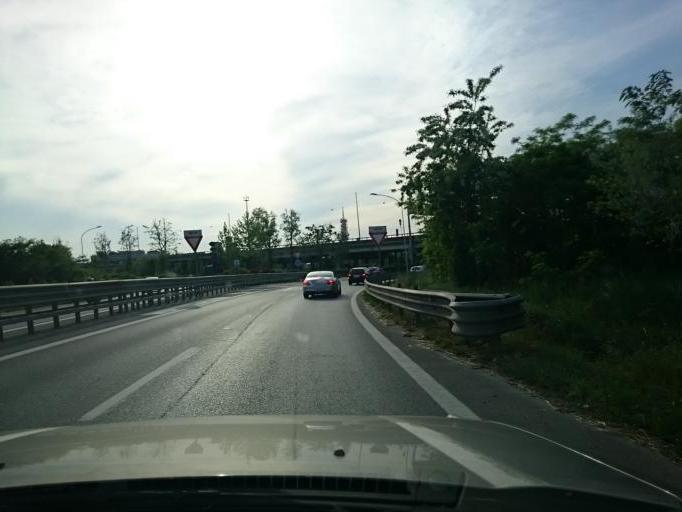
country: IT
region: Veneto
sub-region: Provincia di Venezia
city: Zelarino
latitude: 45.5148
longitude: 12.2458
